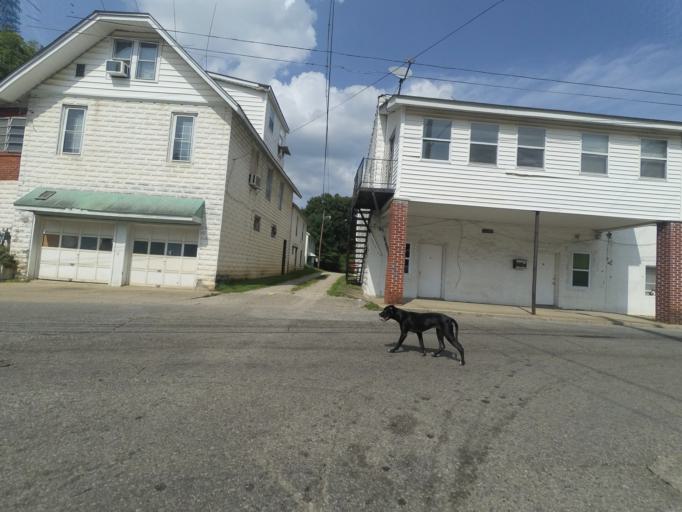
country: US
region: West Virginia
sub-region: Cabell County
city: Huntington
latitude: 38.4154
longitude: -82.4029
